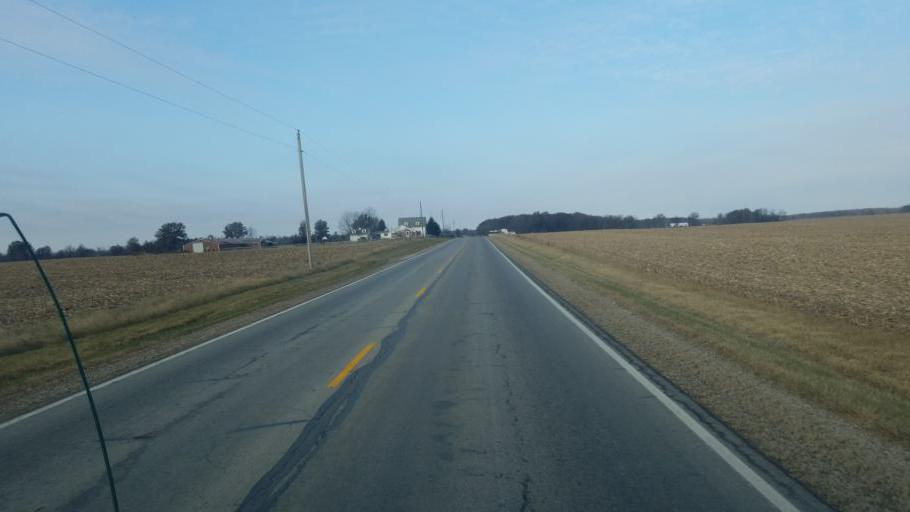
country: US
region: Indiana
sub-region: Adams County
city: Geneva
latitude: 40.5409
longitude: -84.9752
